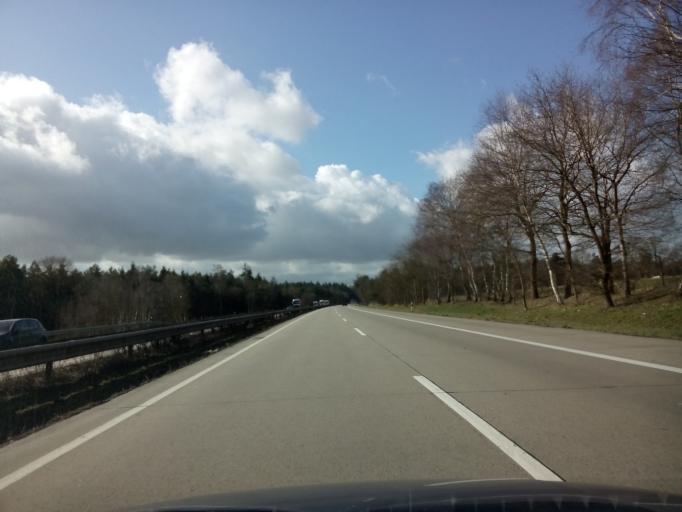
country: DE
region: Lower Saxony
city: Visbek
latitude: 52.8915
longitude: 8.3170
